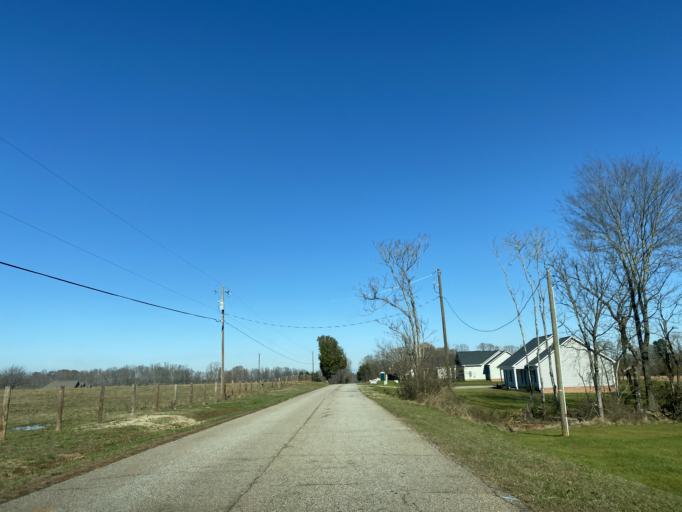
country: US
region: South Carolina
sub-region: Spartanburg County
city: Mayo
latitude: 35.1353
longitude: -81.7864
